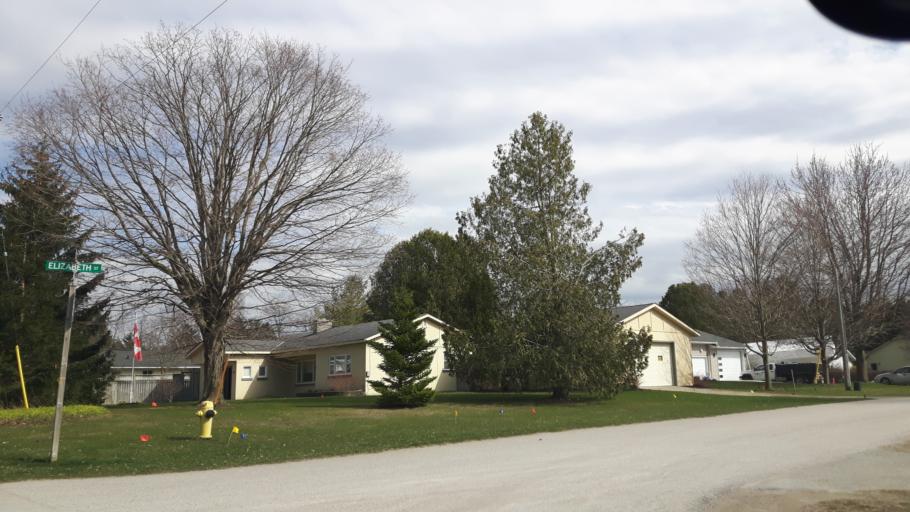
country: CA
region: Ontario
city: Bluewater
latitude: 43.5603
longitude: -81.6913
